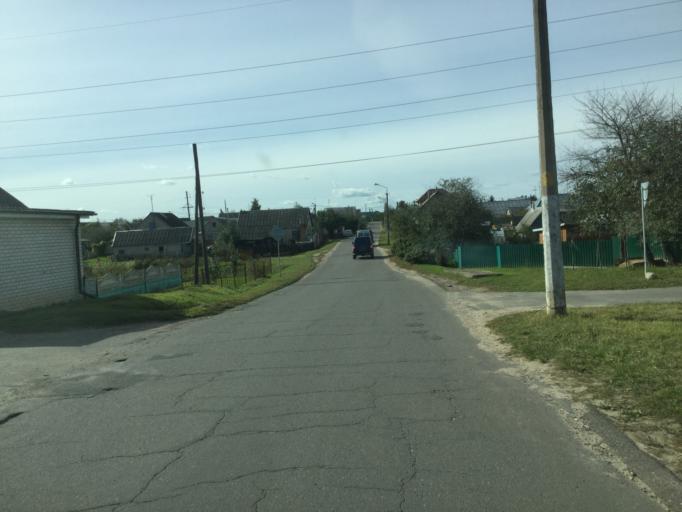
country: BY
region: Vitebsk
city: Orsha
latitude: 54.5476
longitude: 30.4385
